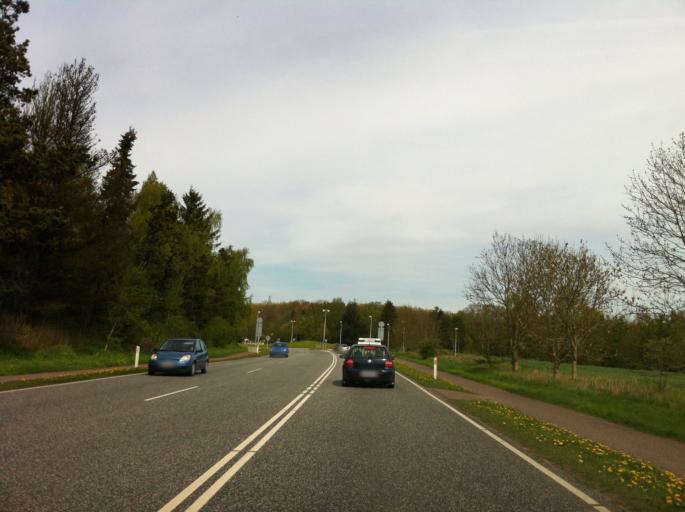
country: DK
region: Capital Region
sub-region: Allerod Kommune
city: Blovstrod
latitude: 55.8925
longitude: 12.3700
